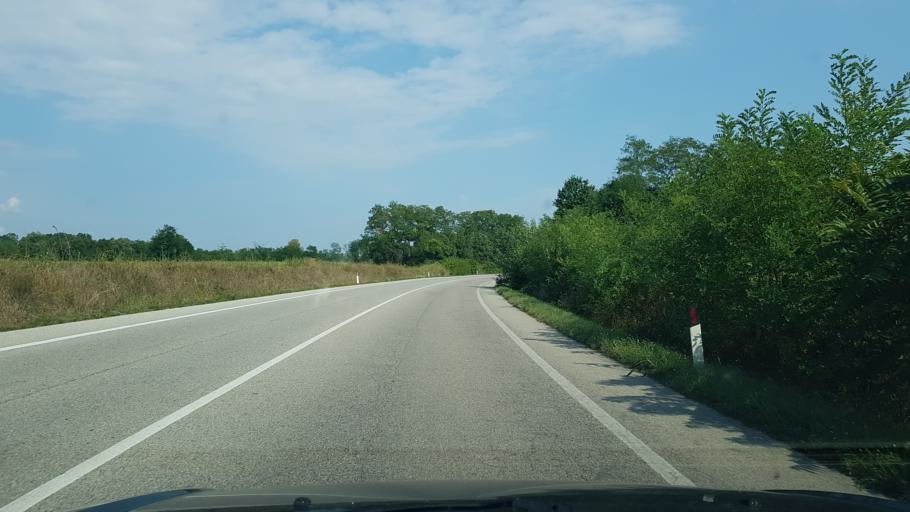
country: IT
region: Friuli Venezia Giulia
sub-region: Provincia di Udine
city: Colloredo di Prato
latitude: 46.0574
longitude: 13.1448
